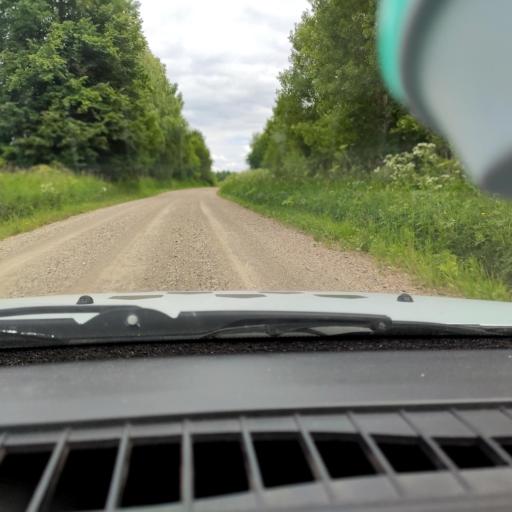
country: RU
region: Perm
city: Suksun
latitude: 57.2111
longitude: 57.6656
